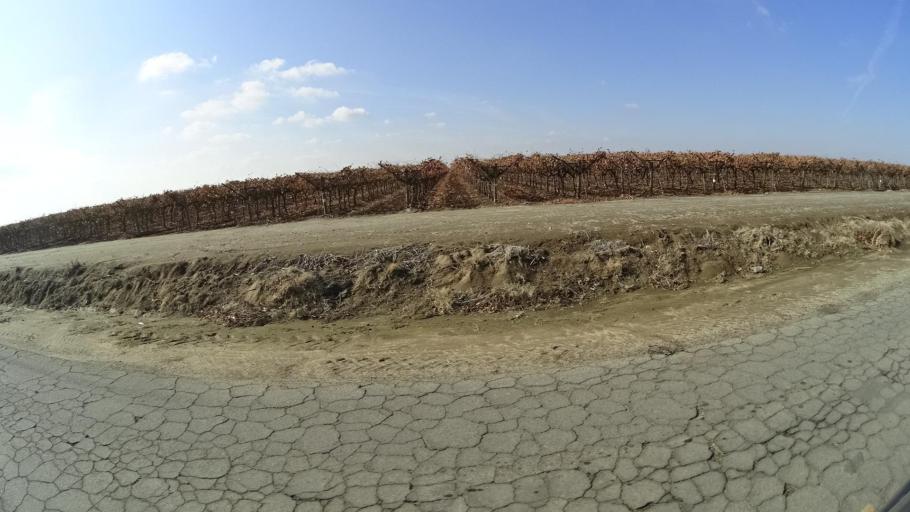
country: US
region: California
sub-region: Kern County
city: Arvin
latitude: 35.2489
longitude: -118.7886
